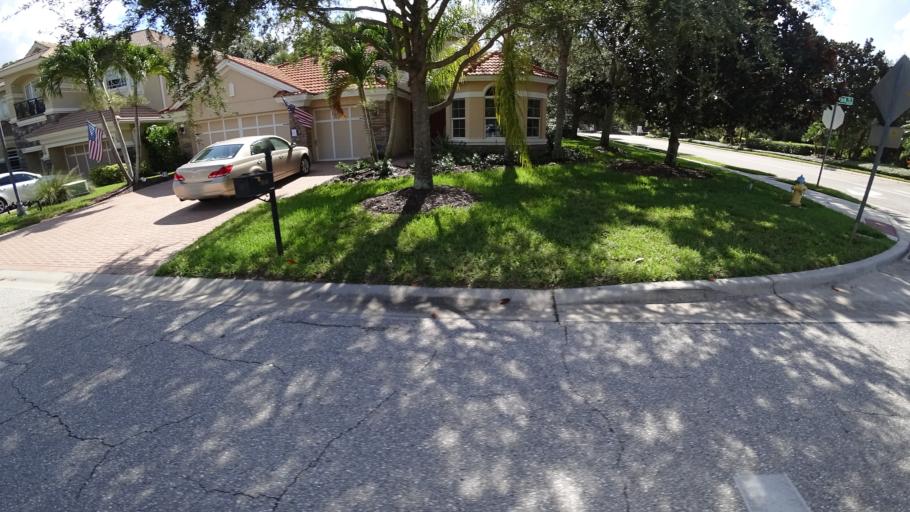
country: US
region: Florida
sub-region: Sarasota County
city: Desoto Lakes
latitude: 27.3928
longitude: -82.4962
